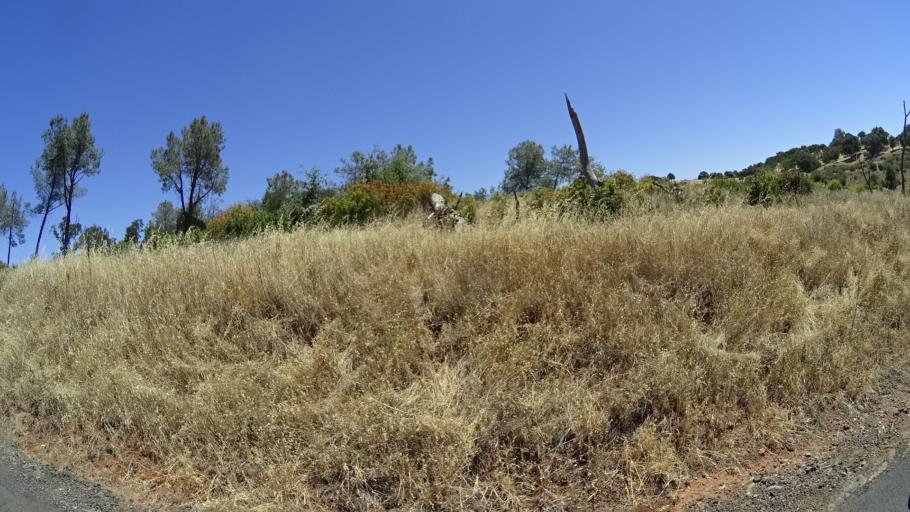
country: US
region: California
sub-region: Calaveras County
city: Copperopolis
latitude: 37.9815
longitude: -120.6959
